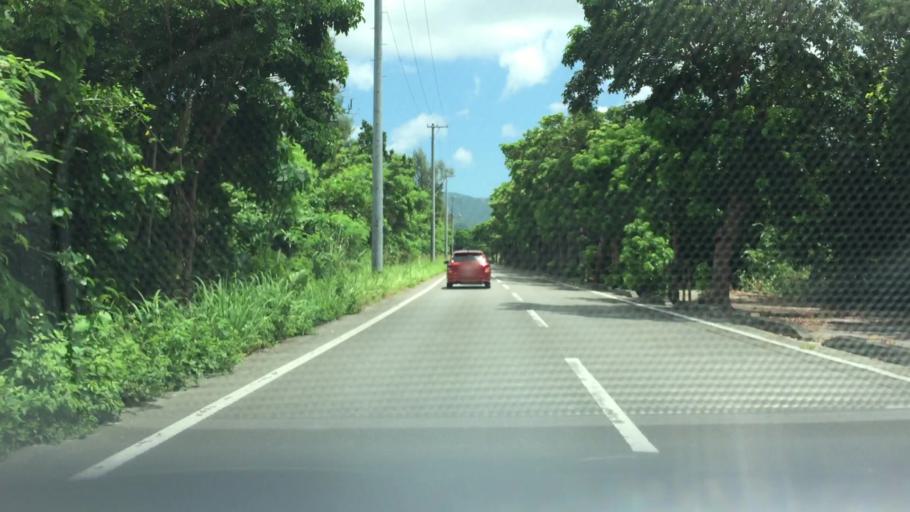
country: JP
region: Okinawa
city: Ishigaki
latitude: 24.3870
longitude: 124.1393
